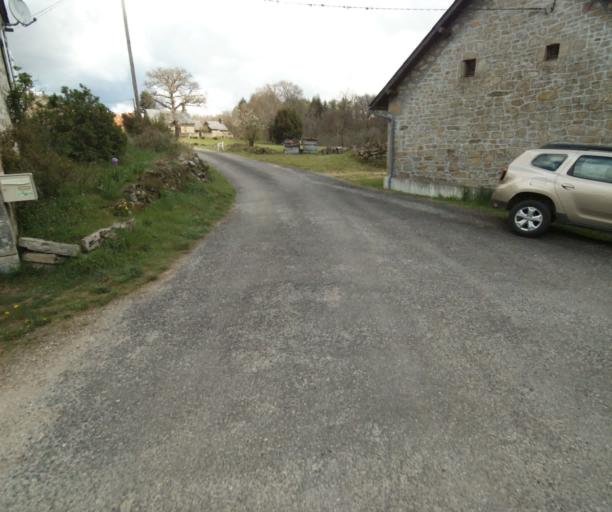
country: FR
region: Limousin
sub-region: Departement de la Correze
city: Correze
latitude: 45.2735
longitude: 1.8971
